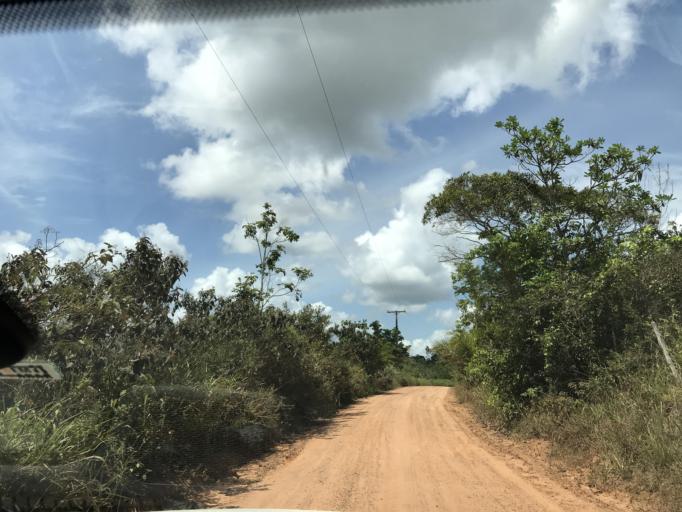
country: BR
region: Bahia
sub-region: Entre Rios
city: Entre Rios
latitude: -12.2217
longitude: -38.0853
